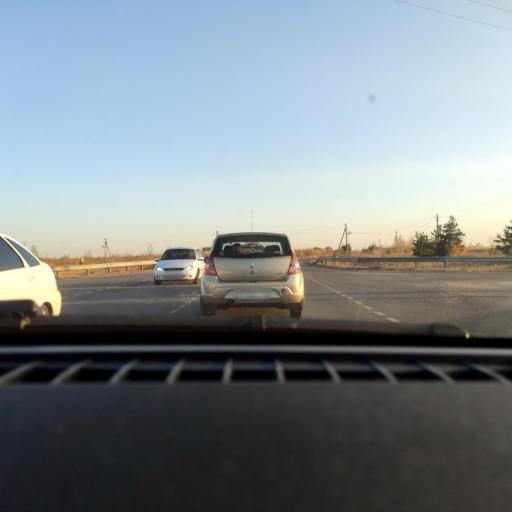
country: RU
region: Voronezj
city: Maslovka
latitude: 51.5777
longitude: 39.2660
